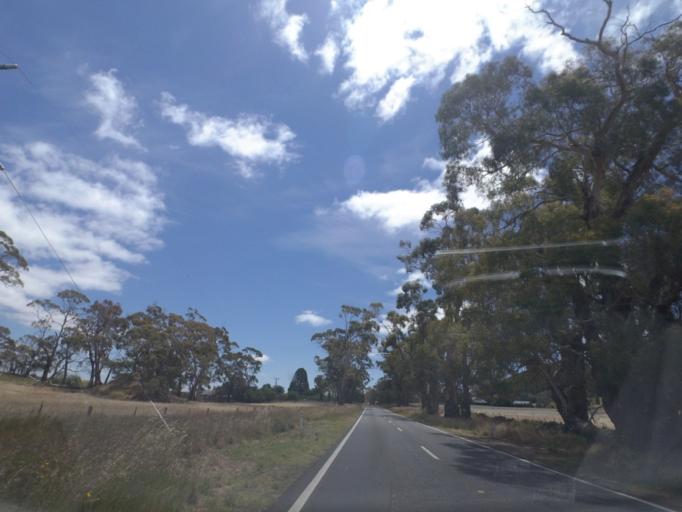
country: AU
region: Victoria
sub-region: Mount Alexander
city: Castlemaine
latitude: -37.2765
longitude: 144.1485
